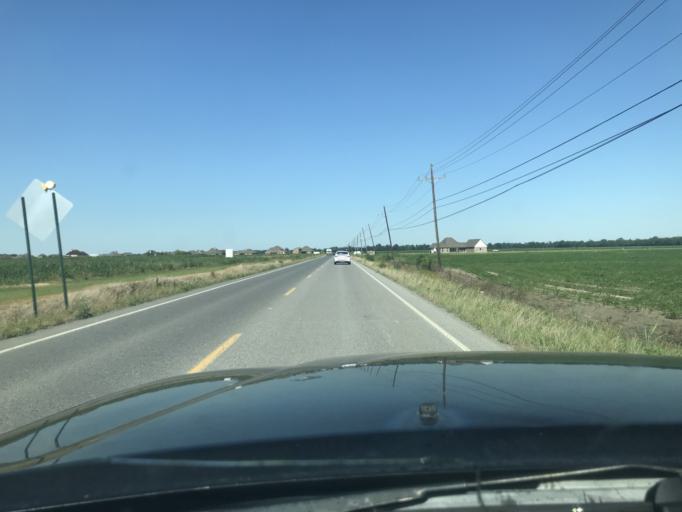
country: US
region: Louisiana
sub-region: West Baton Rouge Parish
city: Brusly
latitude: 30.4685
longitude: -91.3104
